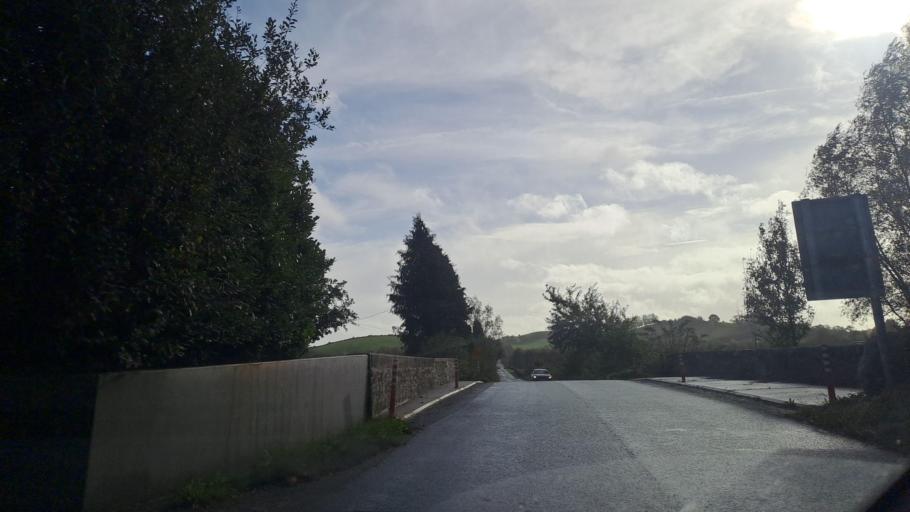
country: IE
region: Ulster
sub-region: County Monaghan
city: Carrickmacross
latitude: 53.9014
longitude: -6.6967
